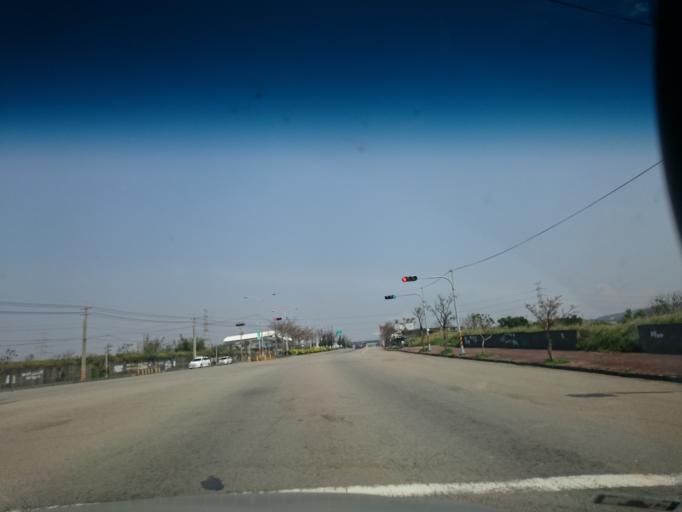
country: TW
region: Taiwan
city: Fengyuan
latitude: 24.2499
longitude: 120.5789
